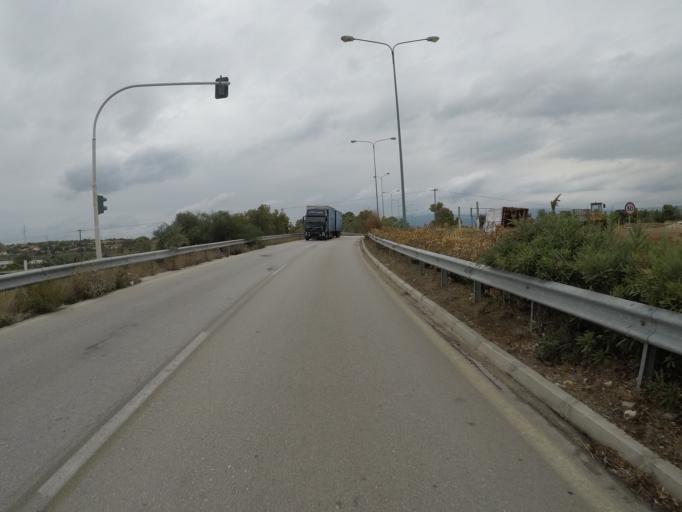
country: GR
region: Peloponnese
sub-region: Nomos Korinthias
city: Kyras Vrysi
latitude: 37.9308
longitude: 22.9937
